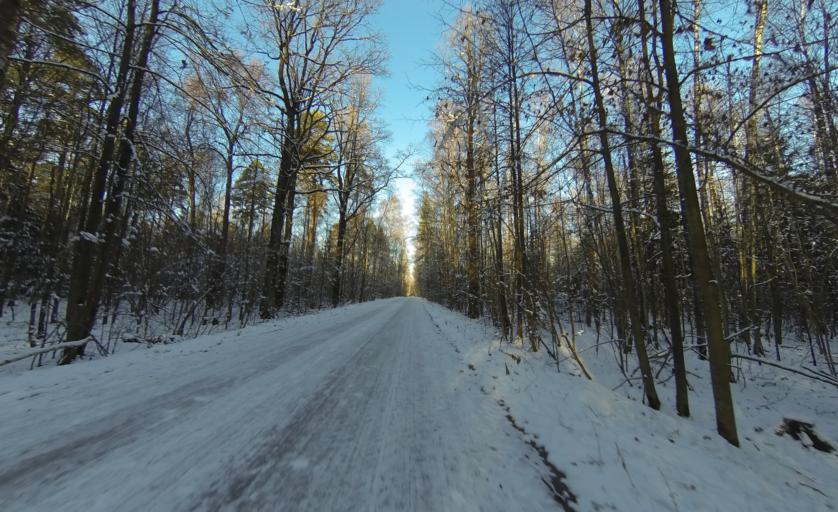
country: RU
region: Moskovskaya
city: Bogorodskoye
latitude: 55.8397
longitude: 37.7270
